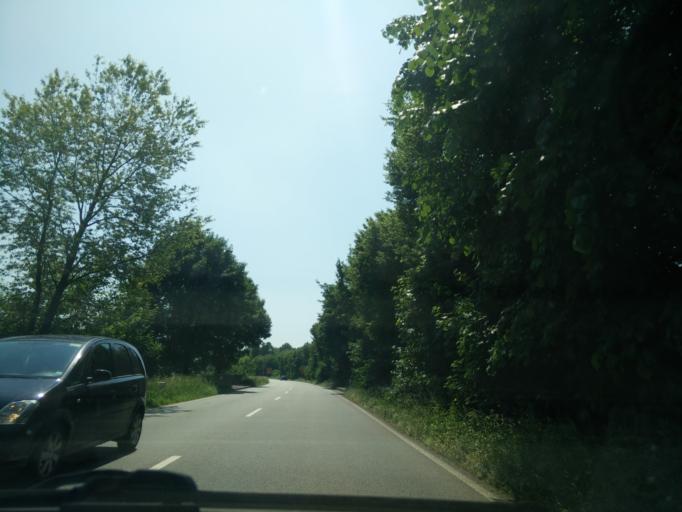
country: DE
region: Bavaria
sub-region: Upper Bavaria
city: Freilassing
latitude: 47.8586
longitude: 12.9826
